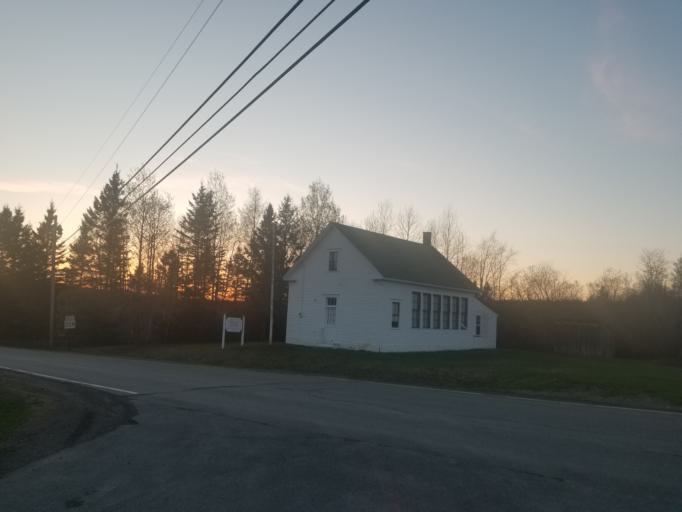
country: US
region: Maine
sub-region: Aroostook County
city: Caribou
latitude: 46.8726
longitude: -68.0713
